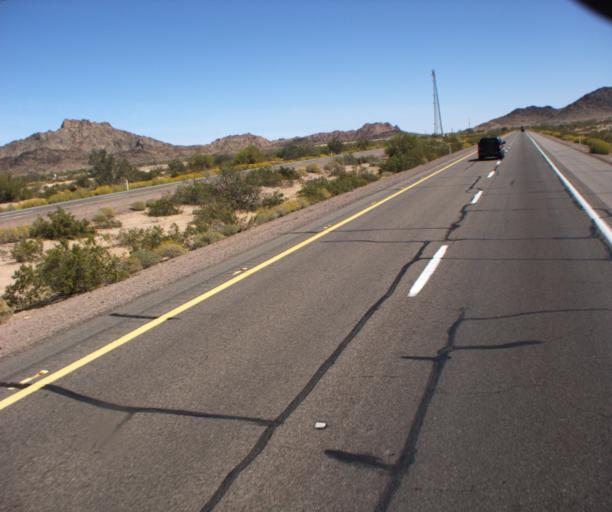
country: US
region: Arizona
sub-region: Yuma County
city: Wellton
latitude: 32.7209
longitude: -113.7721
